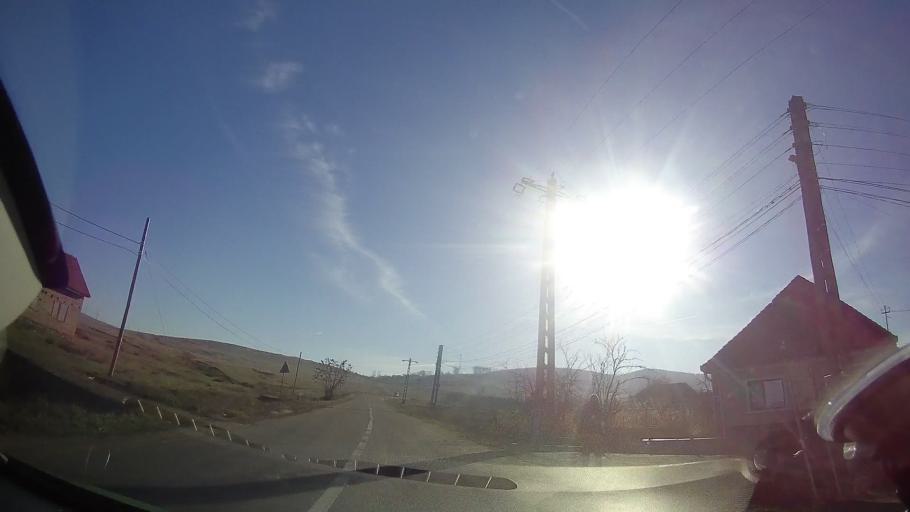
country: RO
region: Bihor
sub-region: Comuna Vadu Crisului
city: Vadu Crisului
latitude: 46.9847
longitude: 22.5294
